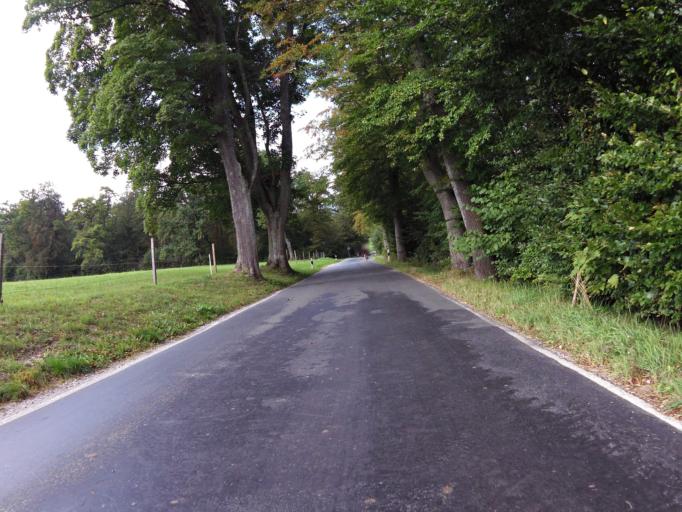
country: DE
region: Bavaria
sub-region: Upper Bavaria
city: Seeshaupt
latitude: 47.8305
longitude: 11.2911
